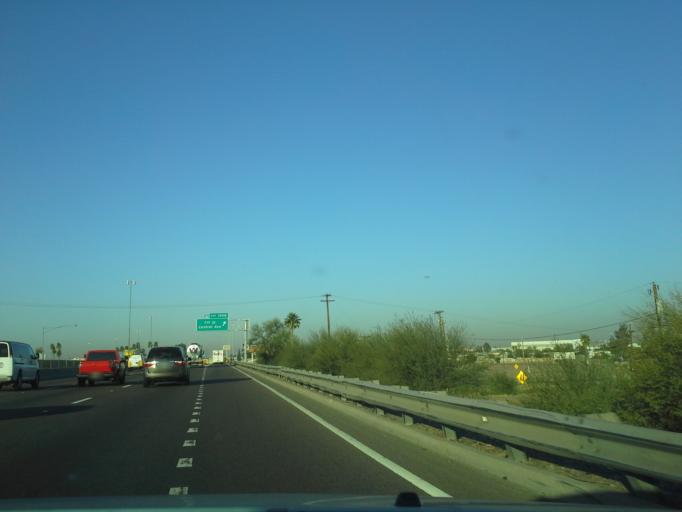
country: US
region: Arizona
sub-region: Maricopa County
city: Phoenix
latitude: 33.4288
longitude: -112.0596
